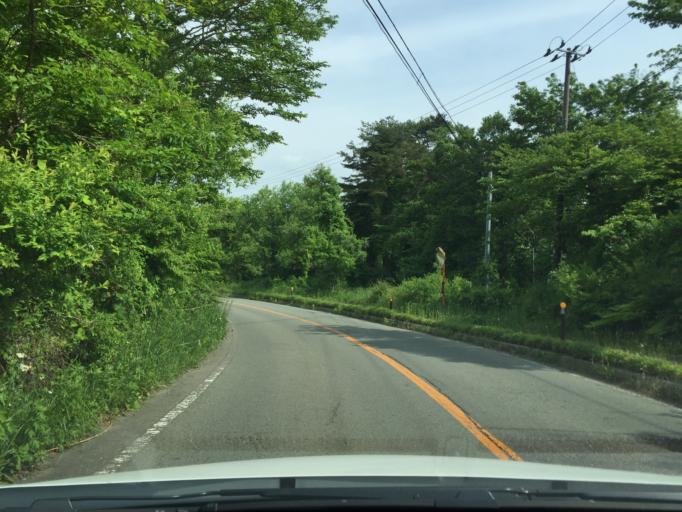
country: JP
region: Fukushima
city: Inawashiro
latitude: 37.6720
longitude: 140.0763
